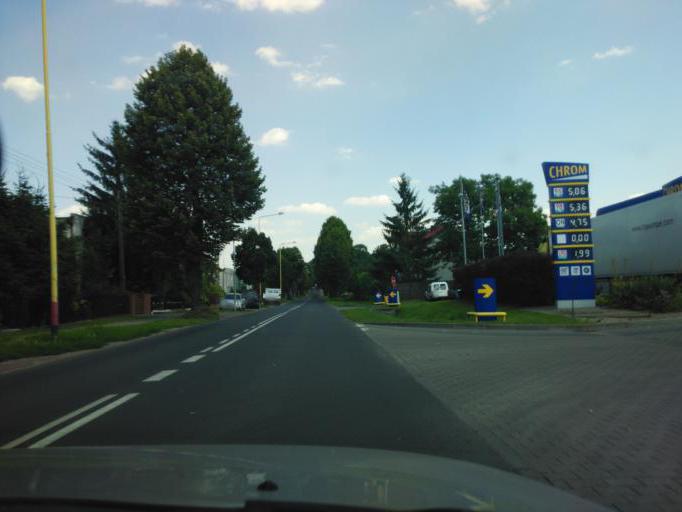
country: PL
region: West Pomeranian Voivodeship
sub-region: Powiat pyrzycki
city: Pyrzyce
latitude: 53.1370
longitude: 14.8994
